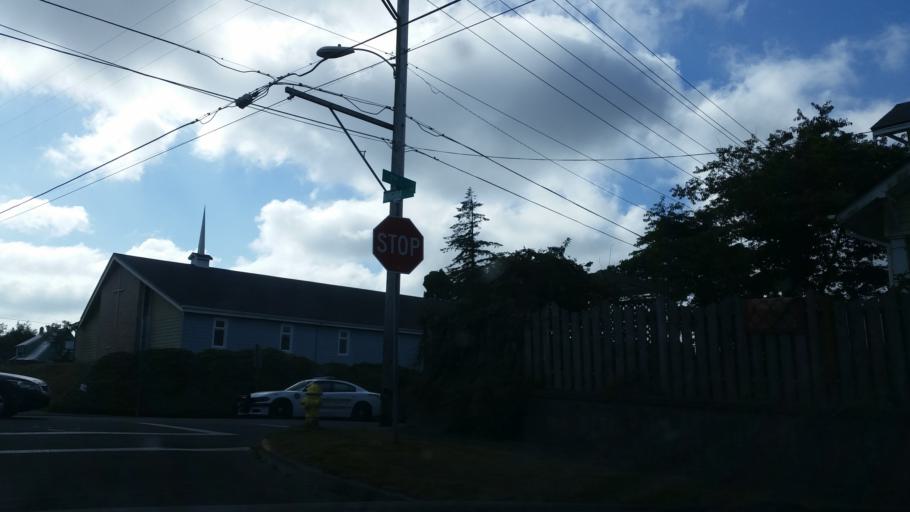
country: US
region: Oregon
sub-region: Clatsop County
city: Astoria
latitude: 46.1812
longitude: -123.8363
